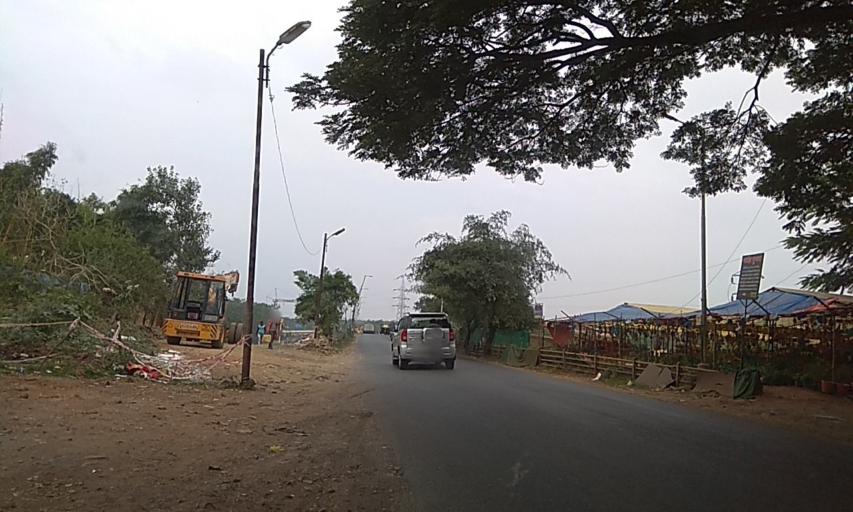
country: IN
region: Maharashtra
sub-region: Pune Division
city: Khadki
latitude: 18.5672
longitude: 73.8076
